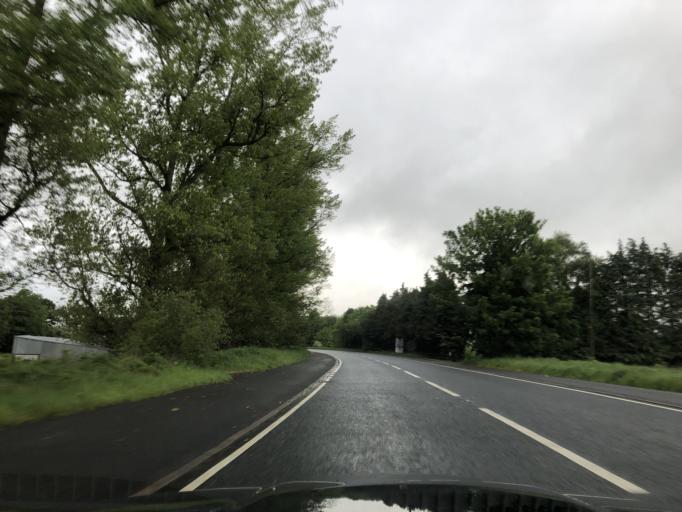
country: GB
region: Northern Ireland
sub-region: Antrim Borough
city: Antrim
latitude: 54.6864
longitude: -6.2234
